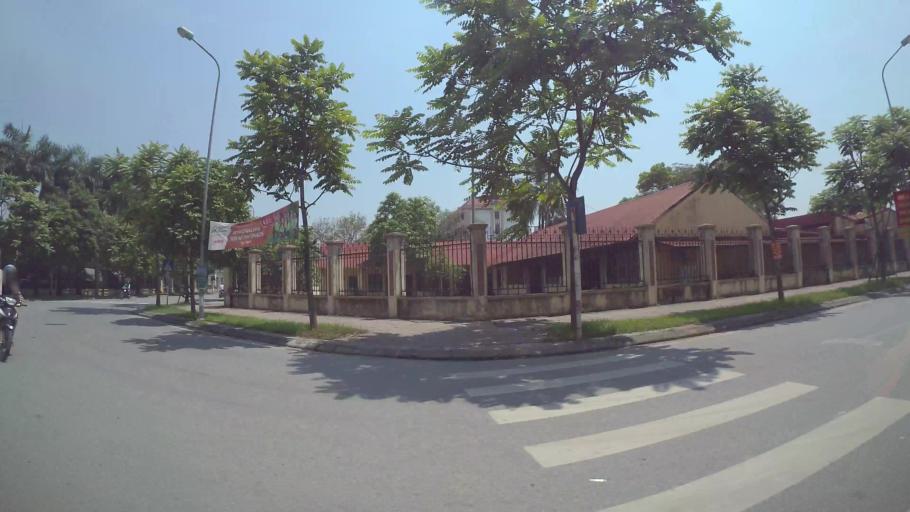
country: VN
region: Ha Noi
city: Hoan Kiem
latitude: 21.0423
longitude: 105.8816
